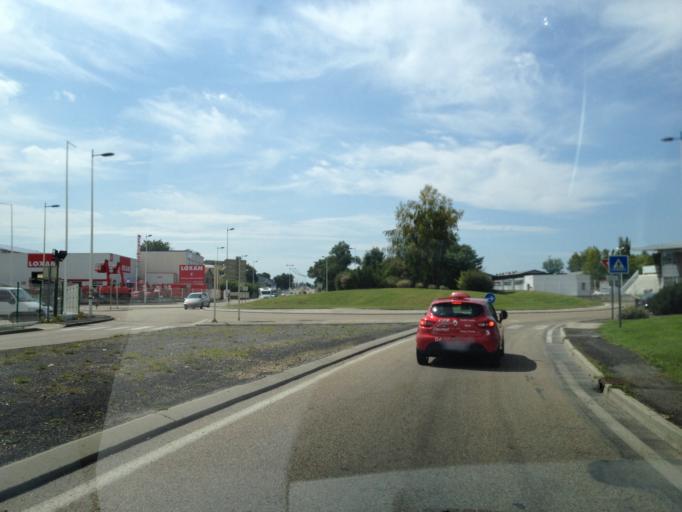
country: FR
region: Languedoc-Roussillon
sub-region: Departement du Gard
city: Ales
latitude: 44.1362
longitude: 4.1050
